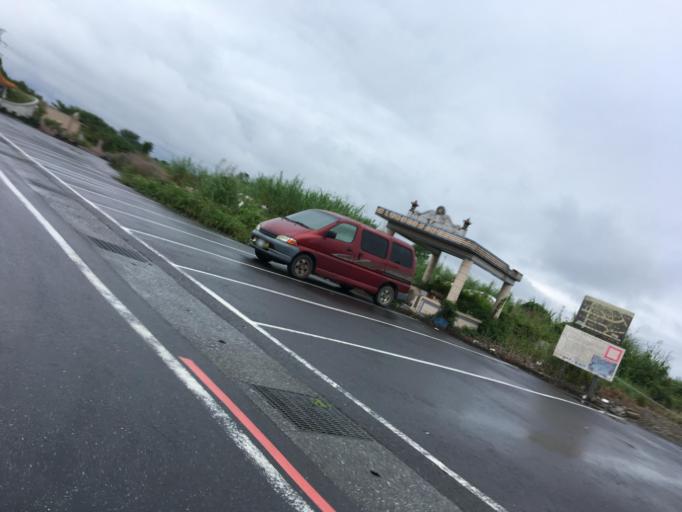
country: TW
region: Taiwan
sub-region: Yilan
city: Yilan
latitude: 24.6631
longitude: 121.7458
